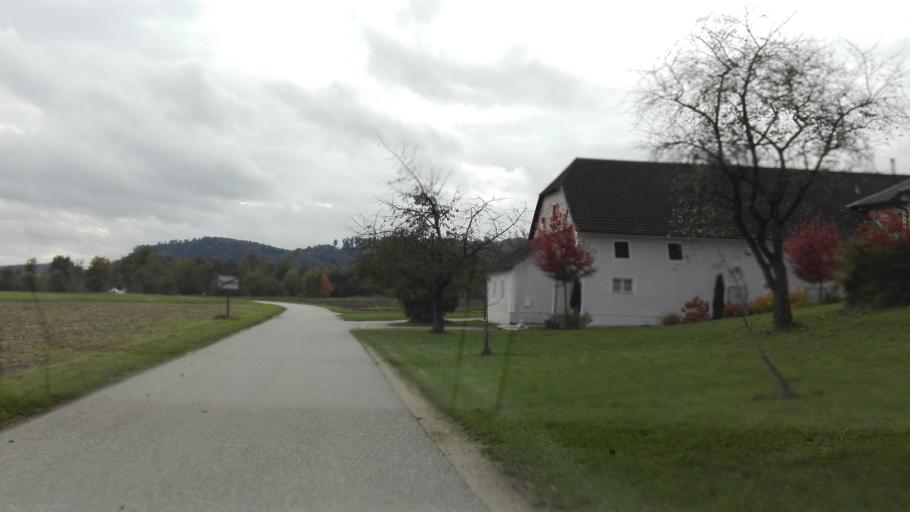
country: AT
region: Upper Austria
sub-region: Politischer Bezirk Urfahr-Umgebung
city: Feldkirchen an der Donau
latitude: 48.3456
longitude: 14.0056
